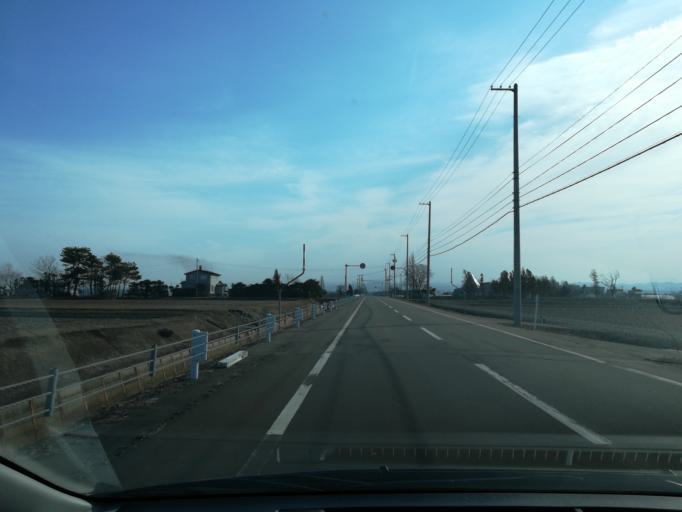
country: JP
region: Hokkaido
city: Iwamizawa
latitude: 43.1783
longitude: 141.6836
